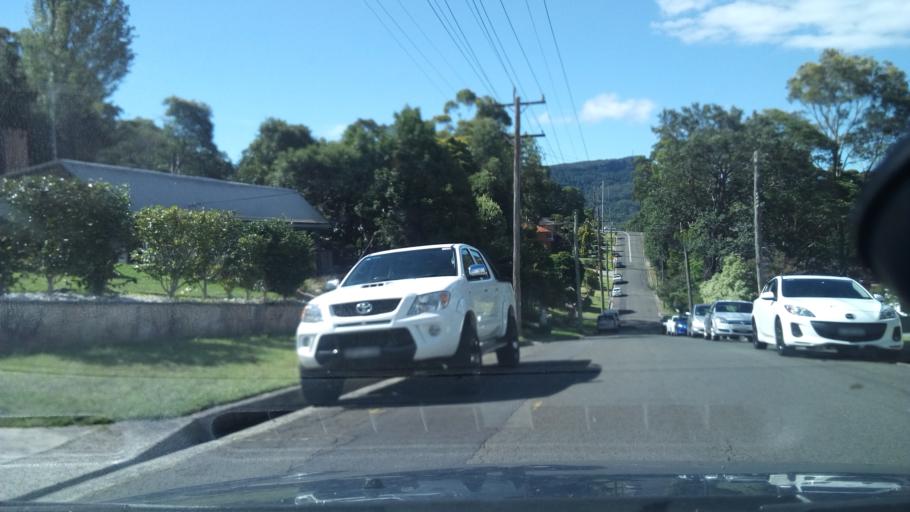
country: AU
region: New South Wales
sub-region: Wollongong
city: Mount Ousley
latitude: -34.3964
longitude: 150.8697
